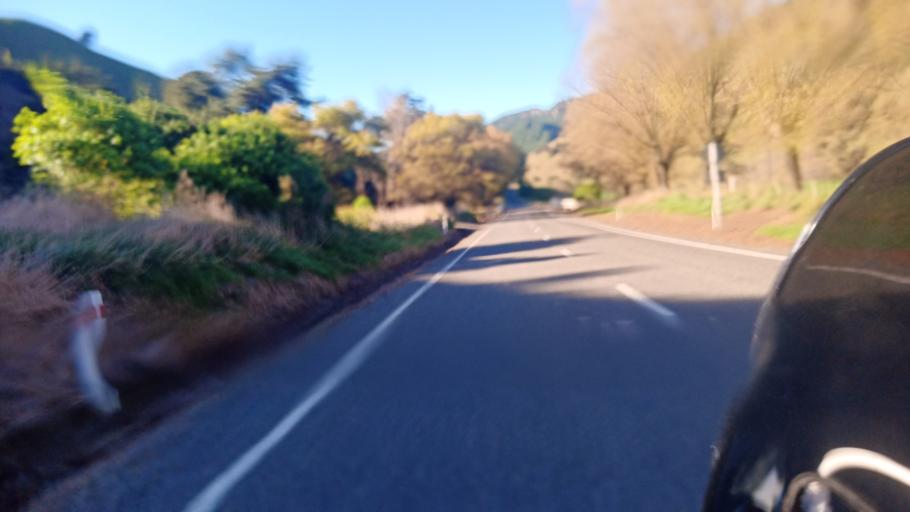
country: NZ
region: Hawke's Bay
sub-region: Wairoa District
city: Wairoa
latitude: -38.8724
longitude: 177.2148
